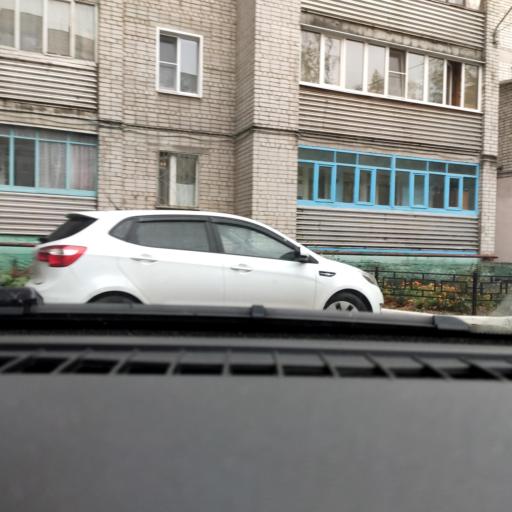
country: RU
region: Voronezj
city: Voronezh
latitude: 51.6413
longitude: 39.2751
